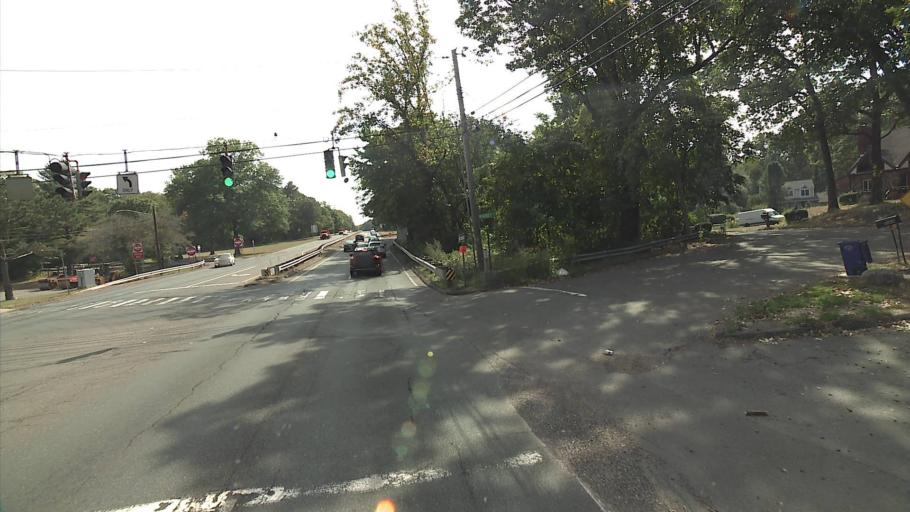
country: US
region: Connecticut
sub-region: New Haven County
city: Orange
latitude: 41.3078
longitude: -73.0365
